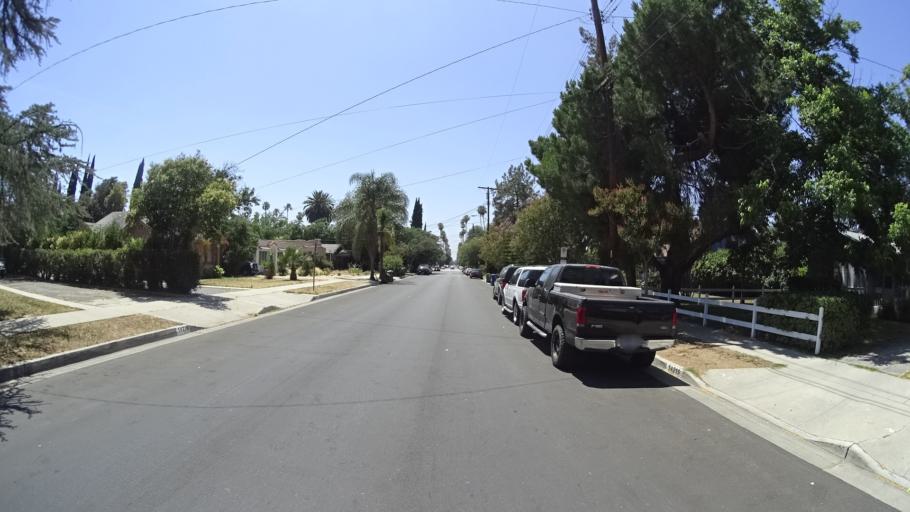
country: US
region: California
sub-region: Los Angeles County
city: Van Nuys
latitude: 34.1907
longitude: -118.4425
